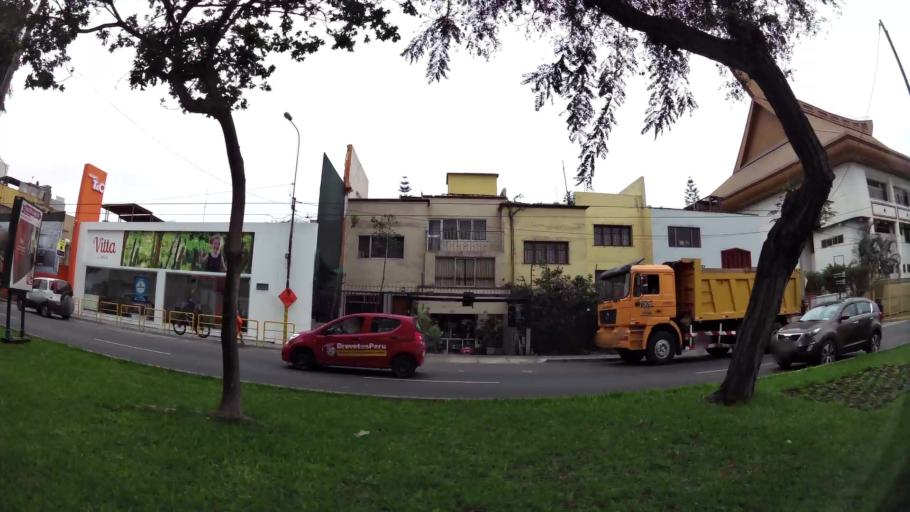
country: PE
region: Lima
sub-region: Lima
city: San Isidro
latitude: -12.0888
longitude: -77.0365
